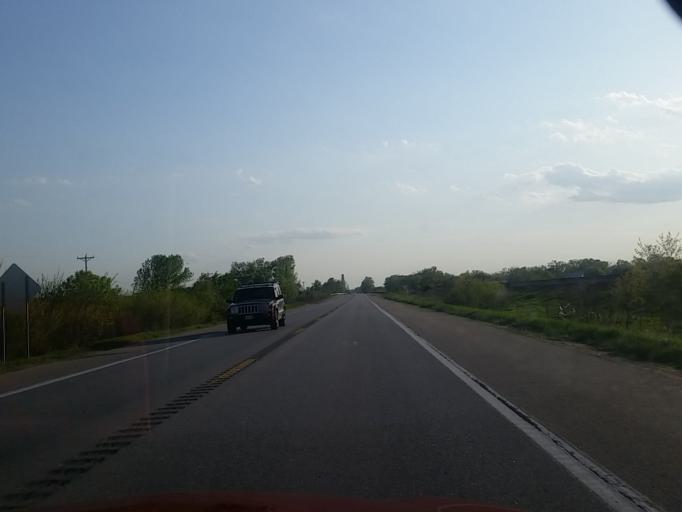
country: US
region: Nebraska
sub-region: Saunders County
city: Ashland
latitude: 41.0702
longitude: -96.3114
